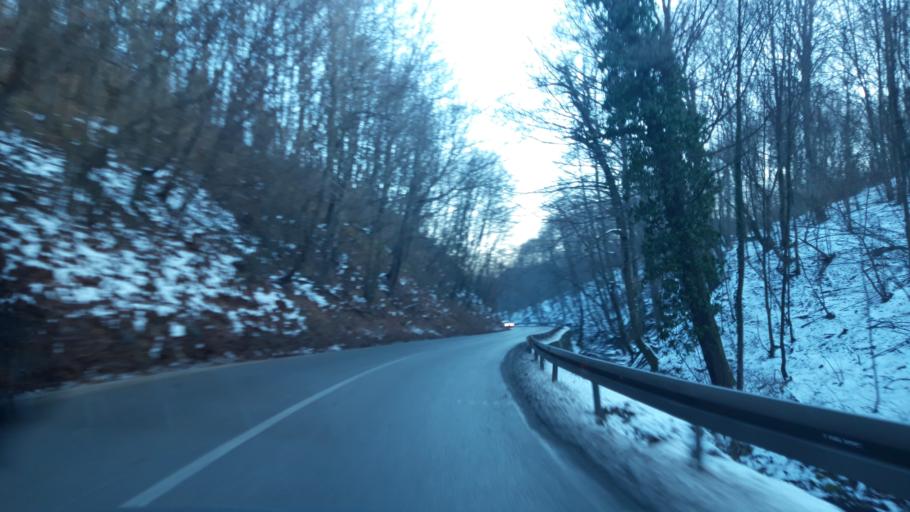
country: BA
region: Republika Srpska
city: Vlasenica
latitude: 44.1842
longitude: 19.0052
